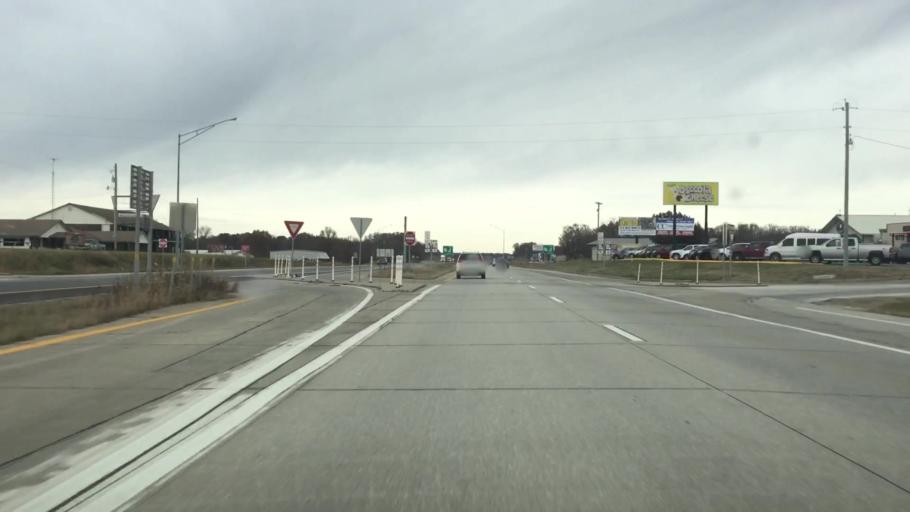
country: US
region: Missouri
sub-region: Saint Clair County
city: Osceola
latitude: 38.0730
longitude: -93.7000
